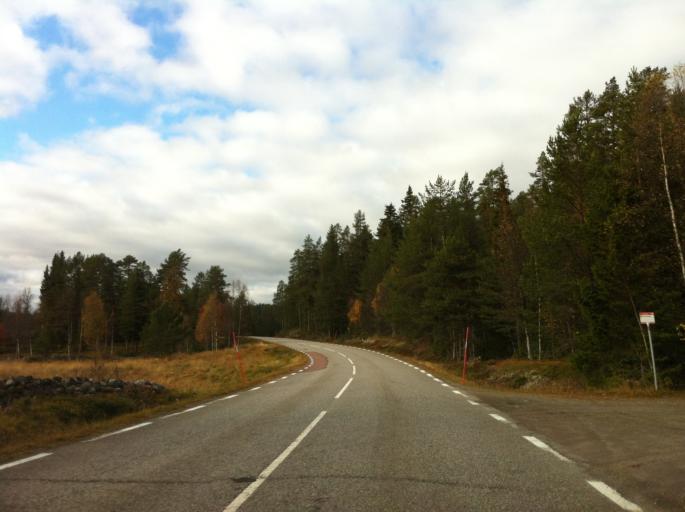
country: NO
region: Hedmark
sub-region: Engerdal
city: Engerdal
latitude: 61.9880
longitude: 12.4651
